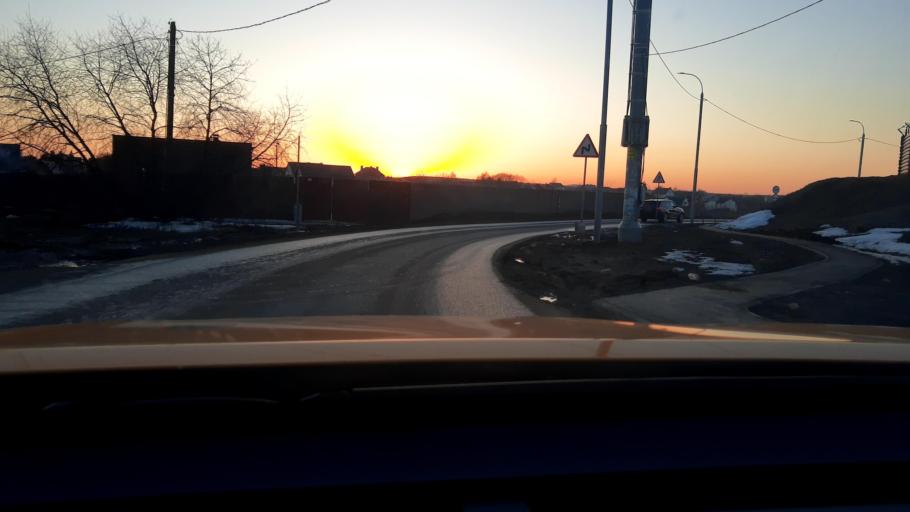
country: RU
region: Moskovskaya
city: Vidnoye
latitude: 55.5187
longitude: 37.7225
